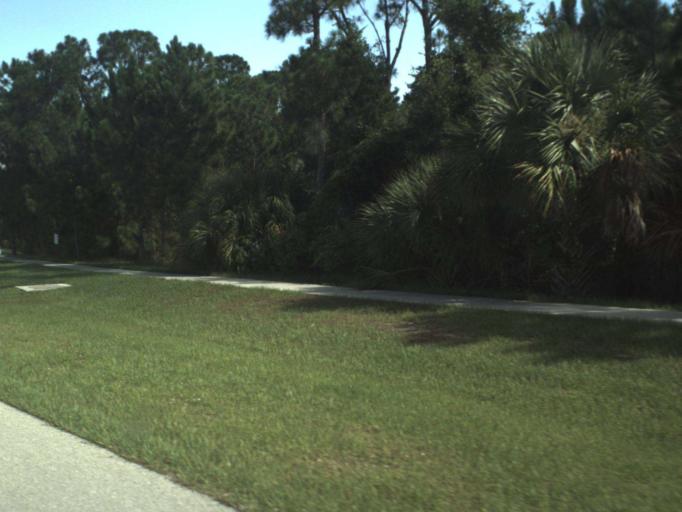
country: US
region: Florida
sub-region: Indian River County
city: Gifford
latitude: 27.6902
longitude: -80.4238
